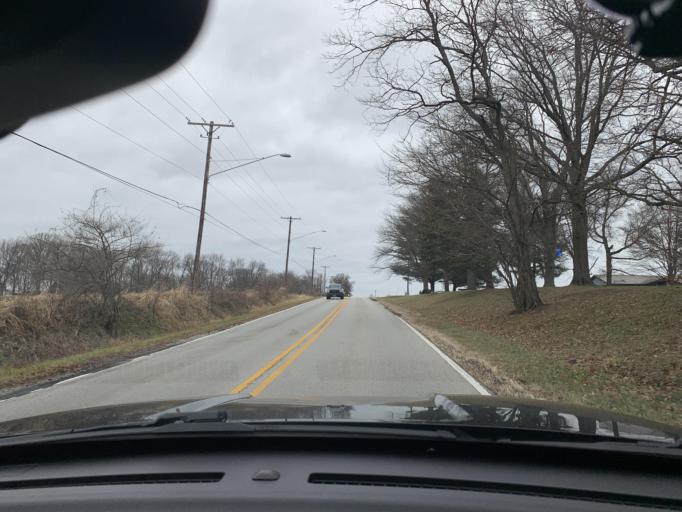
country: US
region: Illinois
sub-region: Sangamon County
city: Jerome
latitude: 39.7312
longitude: -89.6907
